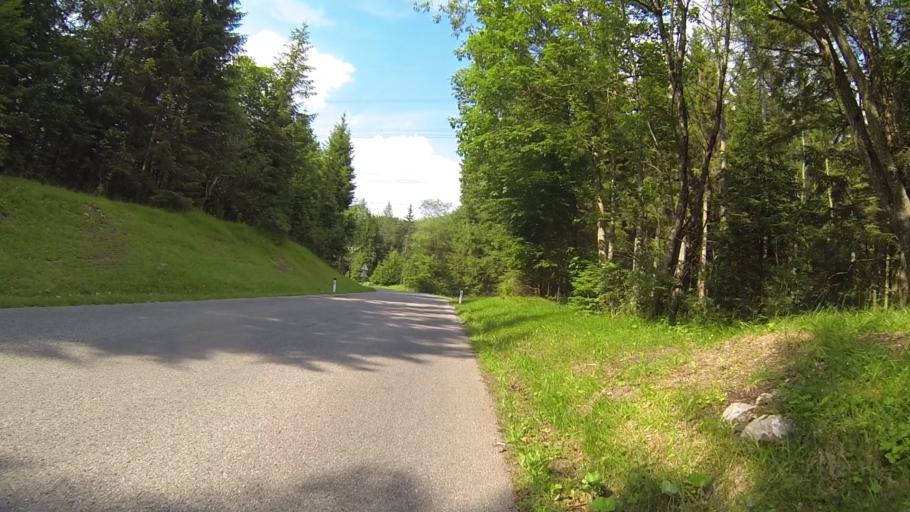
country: AT
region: Tyrol
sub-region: Politischer Bezirk Reutte
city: Pflach
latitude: 47.5243
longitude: 10.7102
